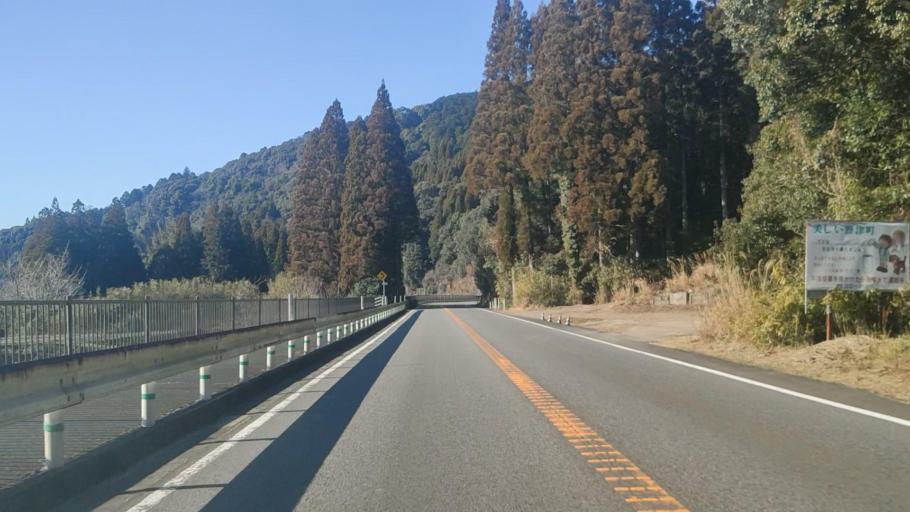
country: JP
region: Oita
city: Usuki
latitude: 33.0072
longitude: 131.7151
